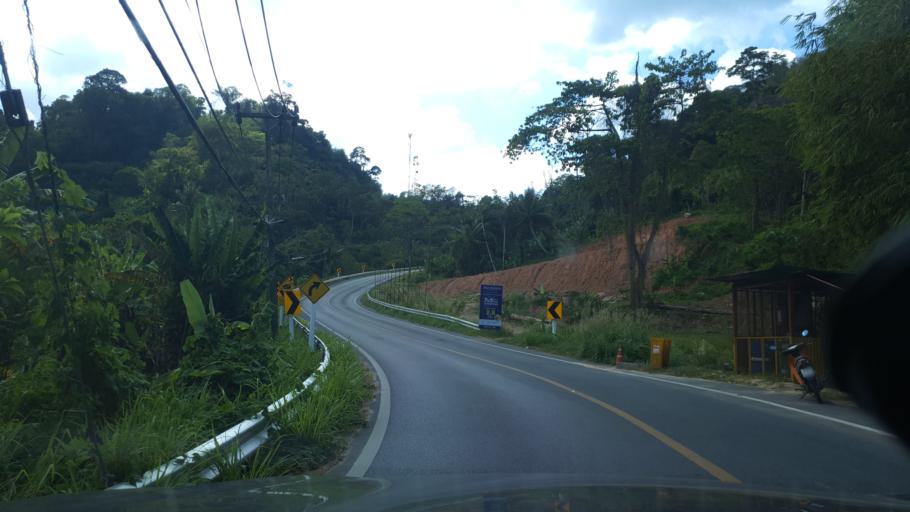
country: TH
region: Phuket
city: Thalang
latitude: 8.0657
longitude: 98.2900
